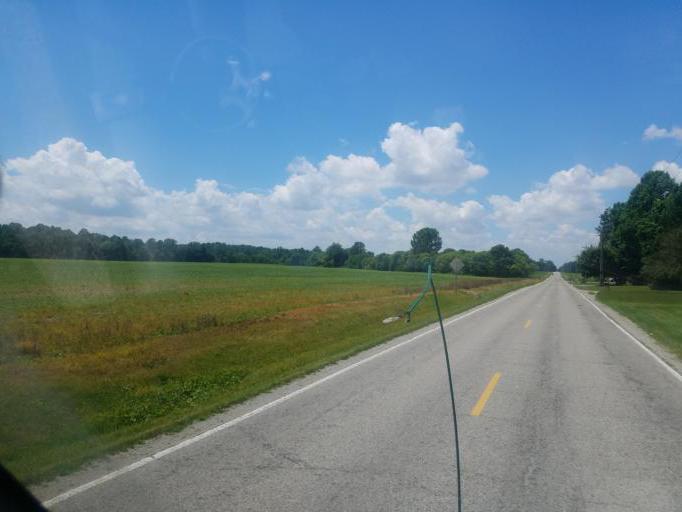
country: US
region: Ohio
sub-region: Huron County
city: Plymouth
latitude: 41.0678
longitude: -82.6127
